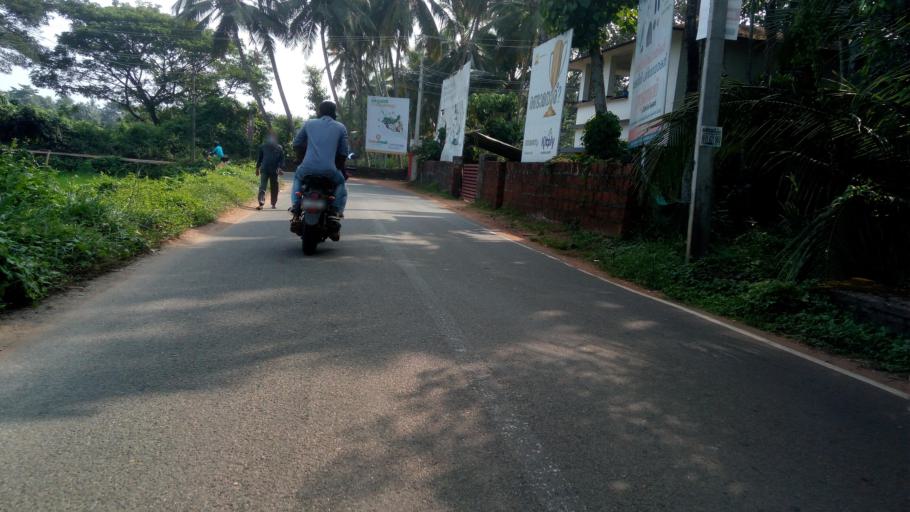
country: IN
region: Kerala
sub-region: Malappuram
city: Malappuram
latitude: 10.9944
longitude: 76.0112
